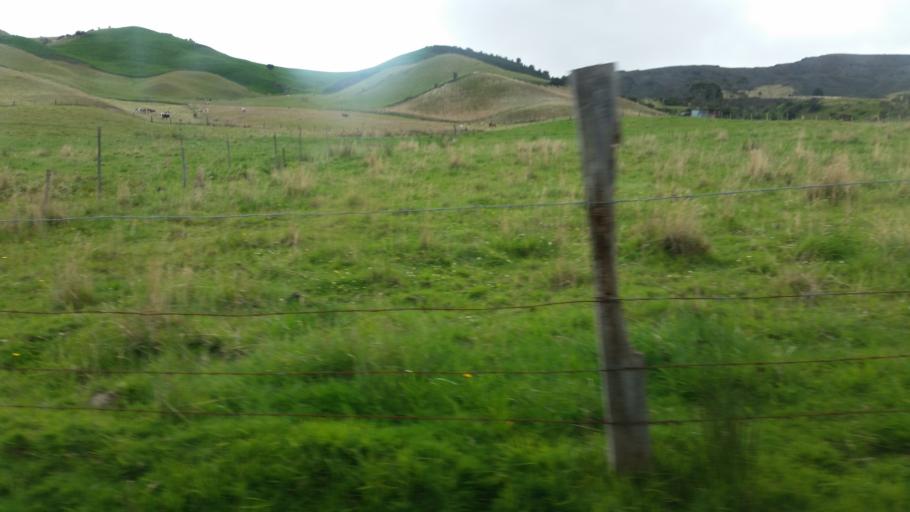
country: CO
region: Cundinamarca
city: Pasca
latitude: 4.3613
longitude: -74.1917
